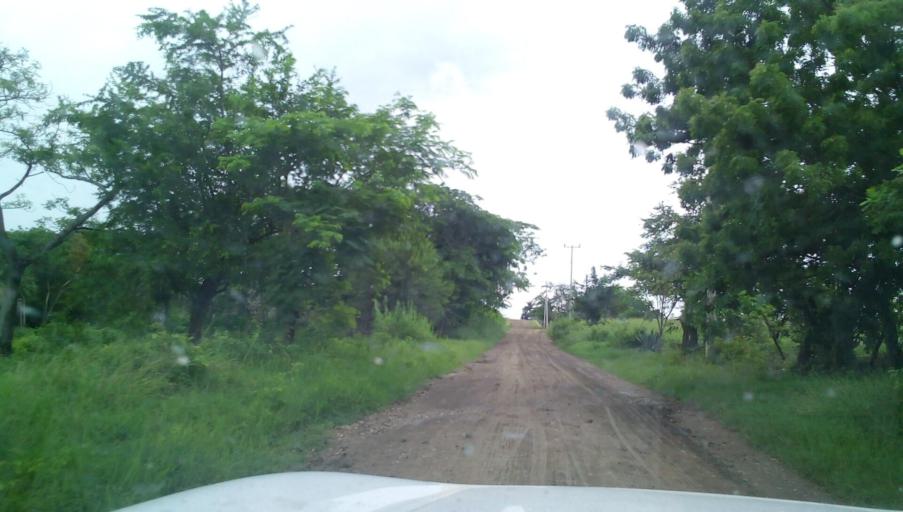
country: MX
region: Veracruz
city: Panuco
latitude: 21.8050
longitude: -98.1060
